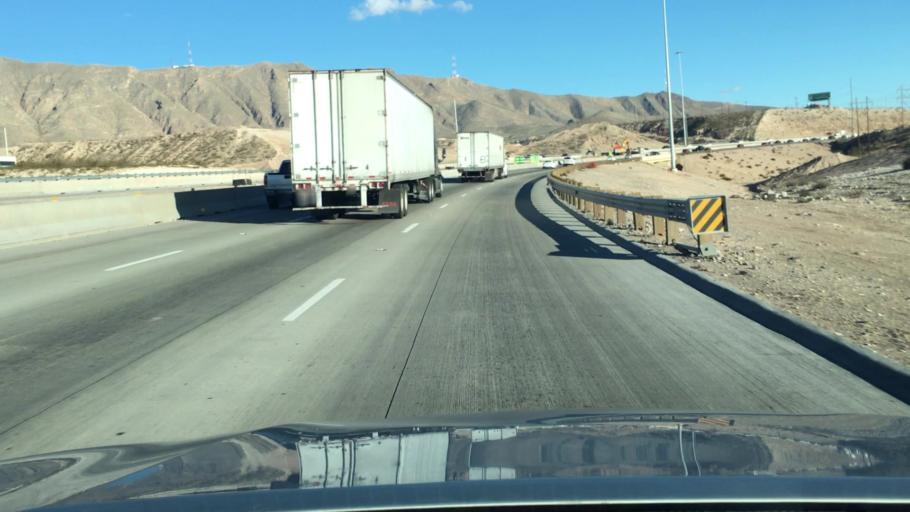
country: US
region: New Mexico
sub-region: Dona Ana County
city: Sunland Park
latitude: 31.8091
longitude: -106.5281
